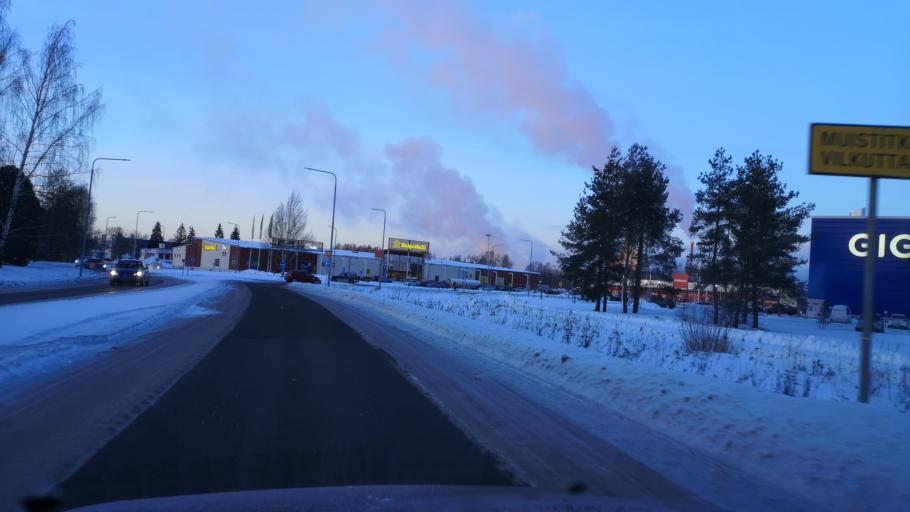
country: FI
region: Satakunta
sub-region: Pori
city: Pori
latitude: 61.4805
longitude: 21.8160
